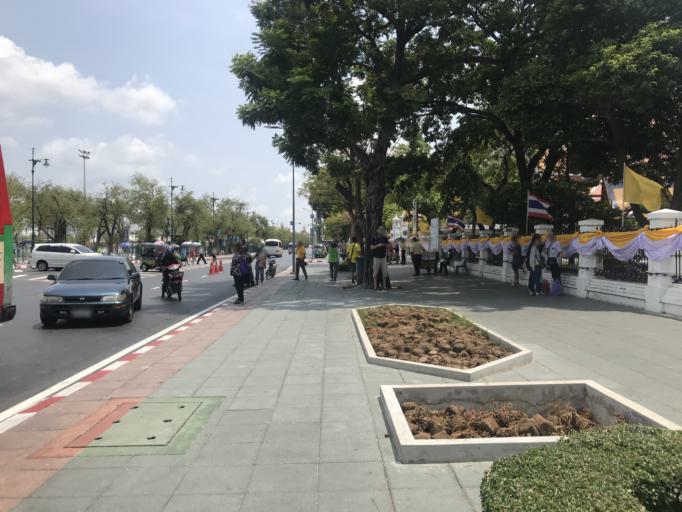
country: TH
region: Bangkok
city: Phra Nakhon
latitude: 13.7579
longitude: 100.4927
